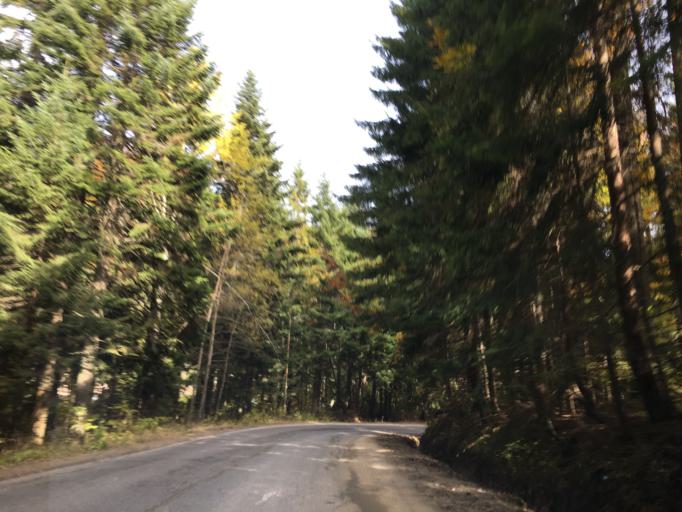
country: BG
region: Sofiya
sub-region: Obshtina Samokov
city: Samokov
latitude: 42.2700
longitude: 23.6122
